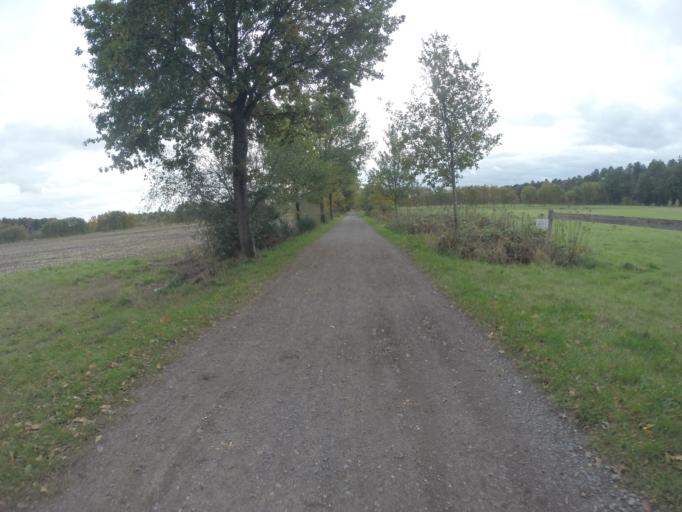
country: BE
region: Flanders
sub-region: Provincie Oost-Vlaanderen
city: Maldegem
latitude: 51.1637
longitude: 3.4598
